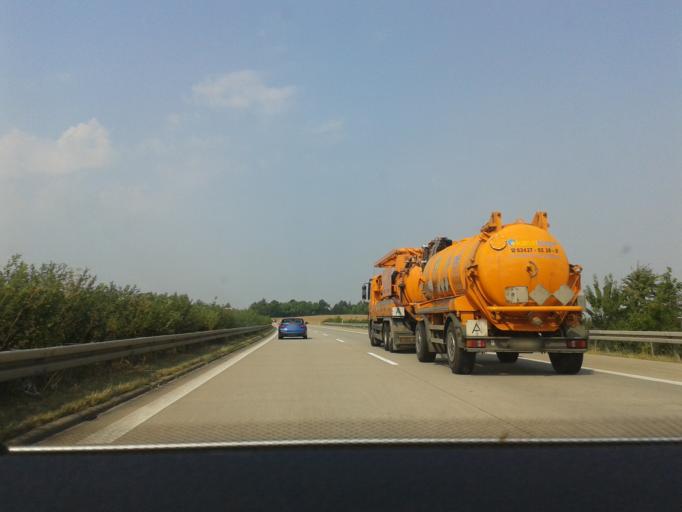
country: DE
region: Saxony
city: Grossweitzschen
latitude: 51.1678
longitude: 13.0797
